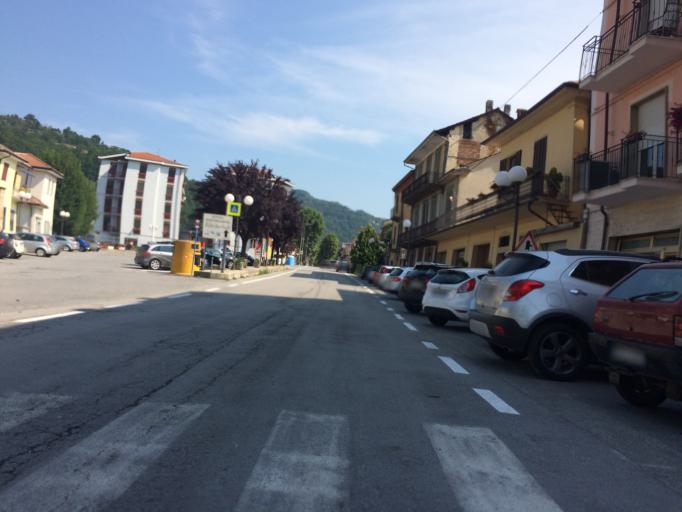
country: IT
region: Piedmont
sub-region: Provincia di Cuneo
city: Cortemilia
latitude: 44.5785
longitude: 8.1956
